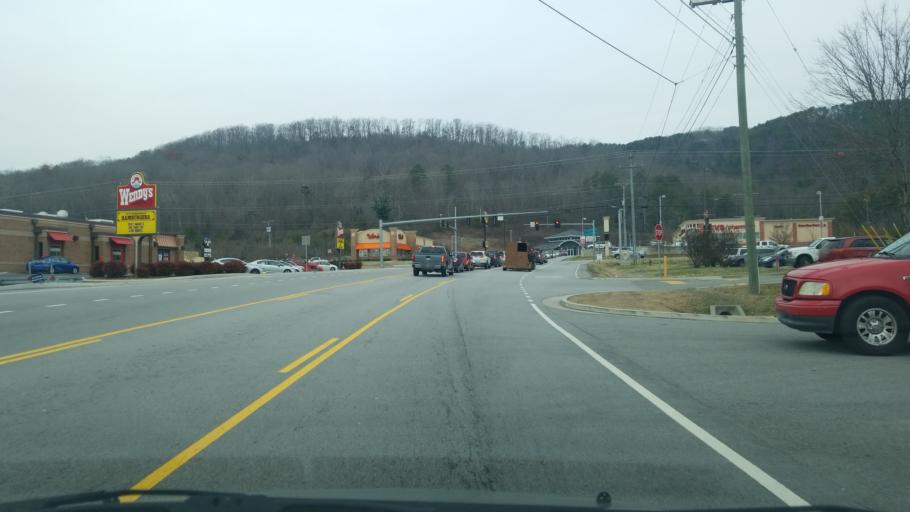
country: US
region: Tennessee
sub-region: Hamilton County
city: Soddy-Daisy
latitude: 35.2365
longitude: -85.1982
